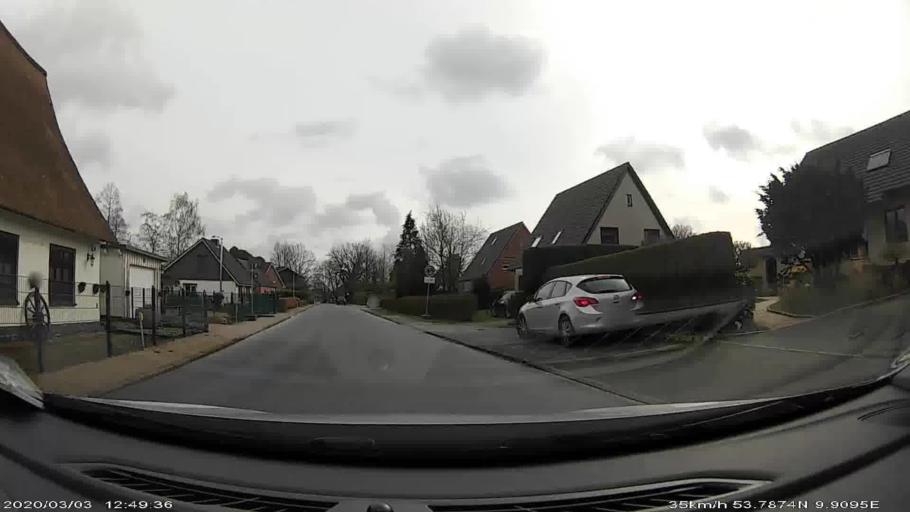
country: DE
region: Schleswig-Holstein
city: Alveslohe
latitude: 53.7868
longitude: 9.9105
